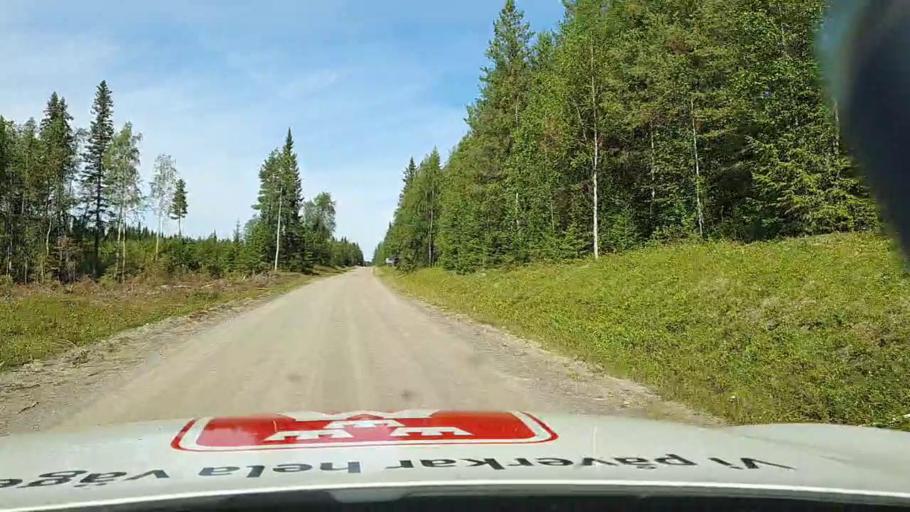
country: SE
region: Jaemtland
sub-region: Stroemsunds Kommun
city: Stroemsund
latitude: 63.7378
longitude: 15.2413
